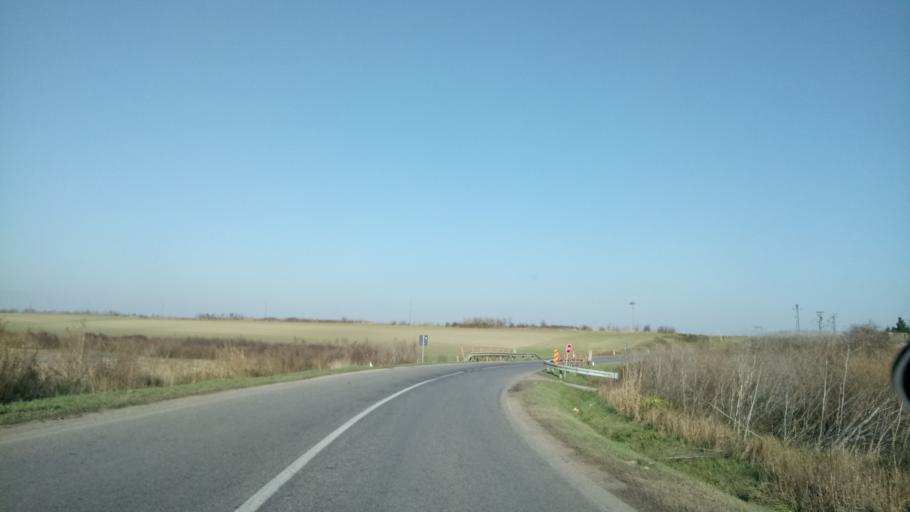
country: RS
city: Ljukovo
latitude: 45.0279
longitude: 20.0466
